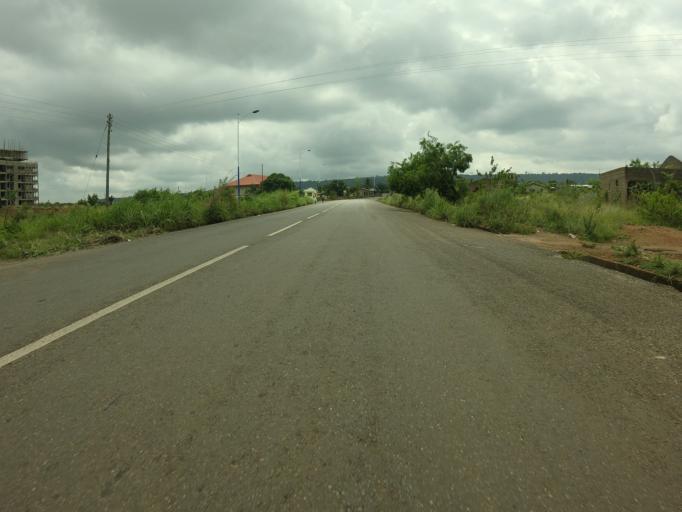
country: GH
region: Volta
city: Ho
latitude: 6.6236
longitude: 0.4920
